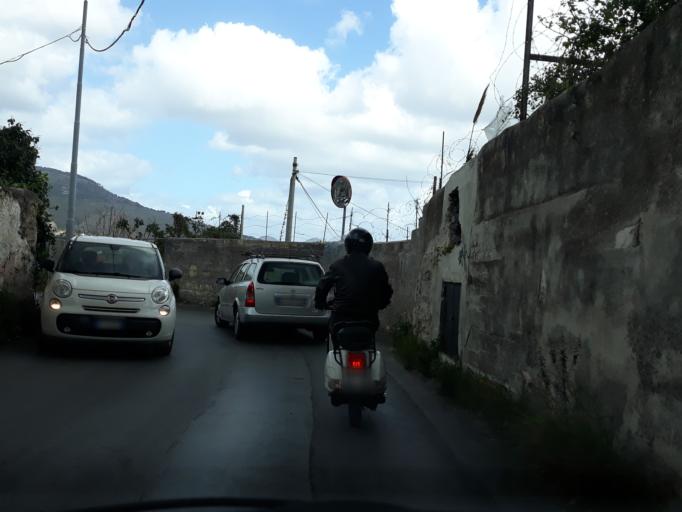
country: IT
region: Sicily
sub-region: Palermo
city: Palermo
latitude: 38.1132
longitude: 13.3080
